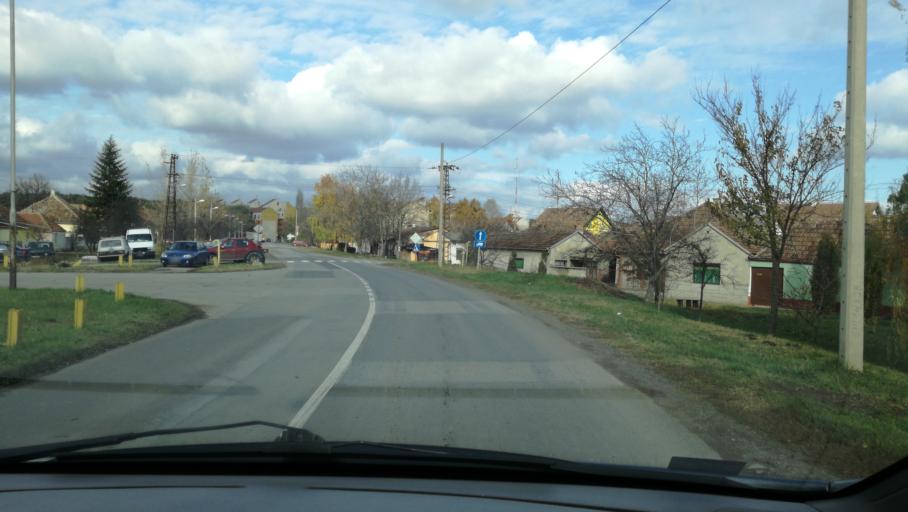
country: RS
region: Autonomna Pokrajina Vojvodina
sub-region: Severnobanatski Okrug
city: Kikinda
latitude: 45.8142
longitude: 20.4496
